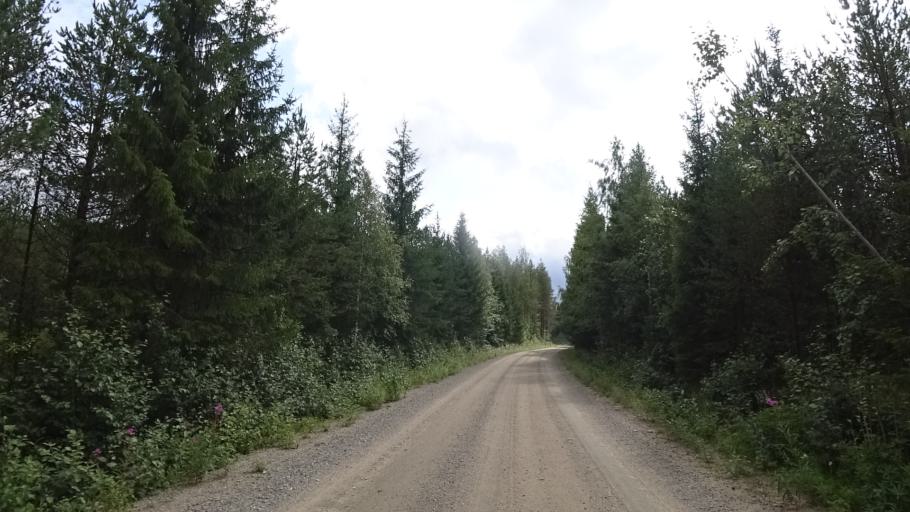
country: FI
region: North Karelia
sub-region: Joensuu
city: Ilomantsi
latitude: 62.9251
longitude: 31.3325
